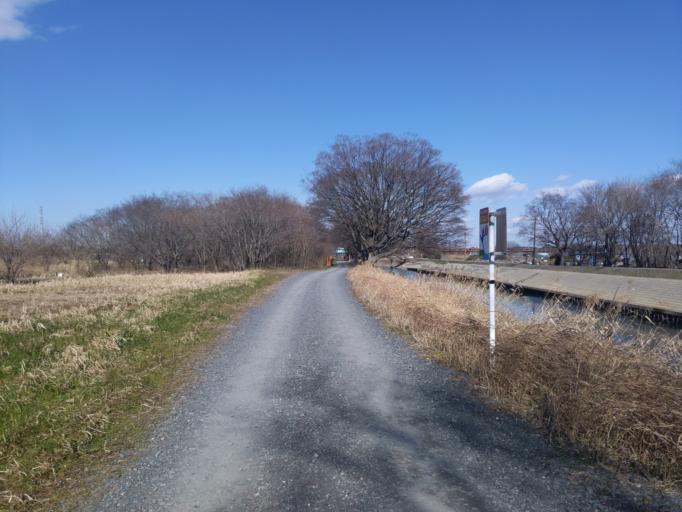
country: JP
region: Saitama
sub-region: Kawaguchi-shi
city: Hatogaya-honcho
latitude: 35.8641
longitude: 139.7136
